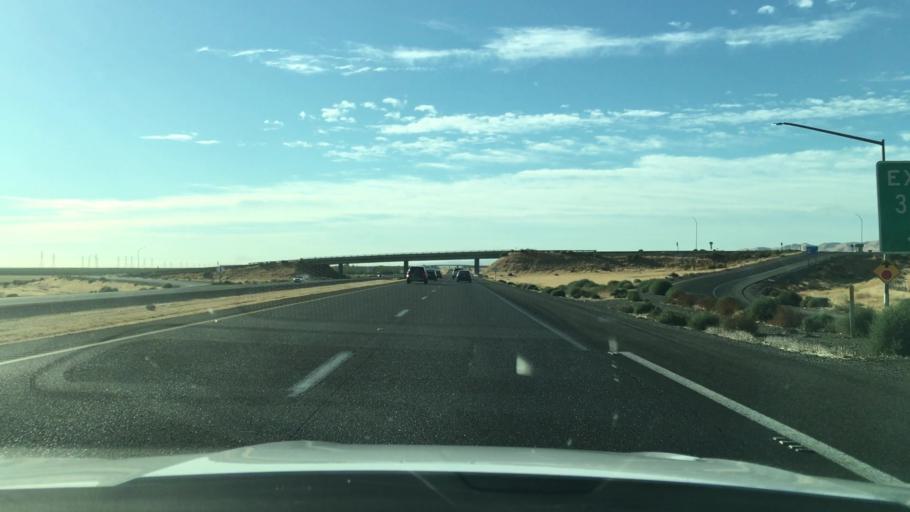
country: US
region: California
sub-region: Merced County
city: South Dos Palos
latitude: 36.8529
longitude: -120.7764
